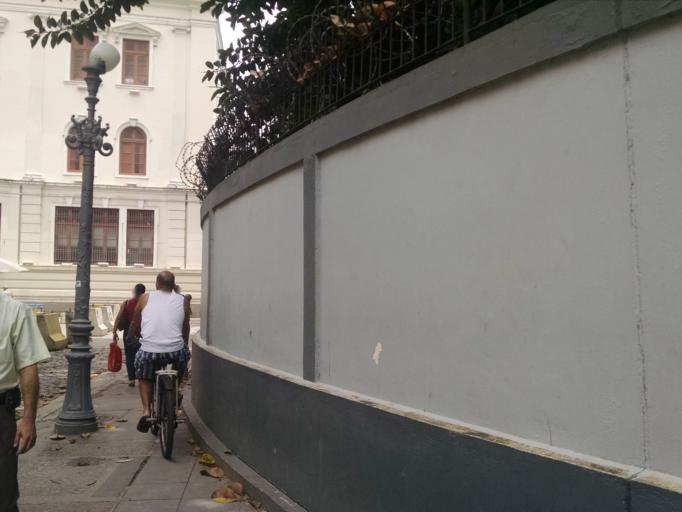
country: BR
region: Rio de Janeiro
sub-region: Rio De Janeiro
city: Rio de Janeiro
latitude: -22.9013
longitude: -43.1752
